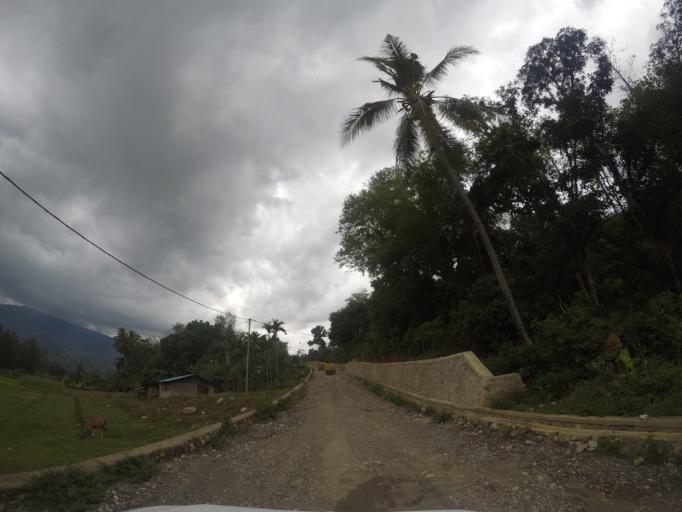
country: TL
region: Bobonaro
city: Maliana
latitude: -8.9752
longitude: 125.2213
